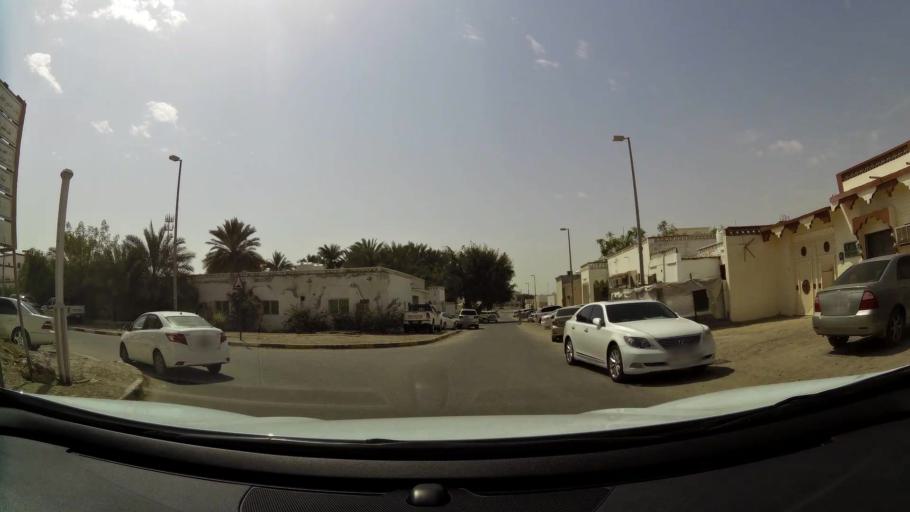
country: AE
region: Abu Dhabi
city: Abu Dhabi
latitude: 24.3024
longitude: 54.6369
